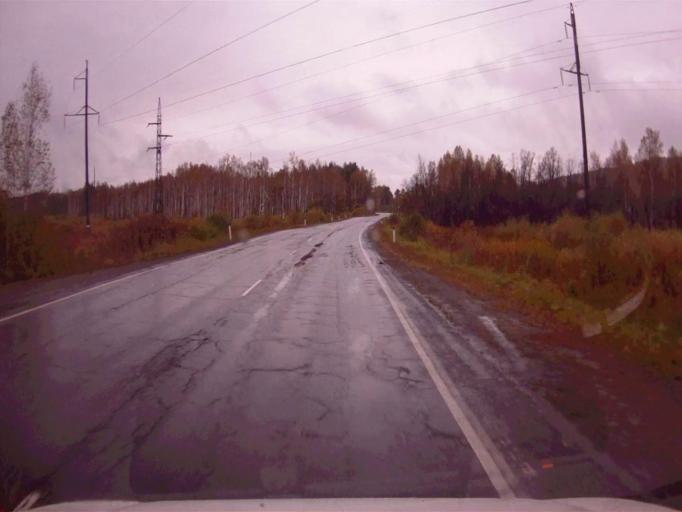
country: RU
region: Chelyabinsk
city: Verkhniy Ufaley
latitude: 55.9927
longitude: 60.3330
